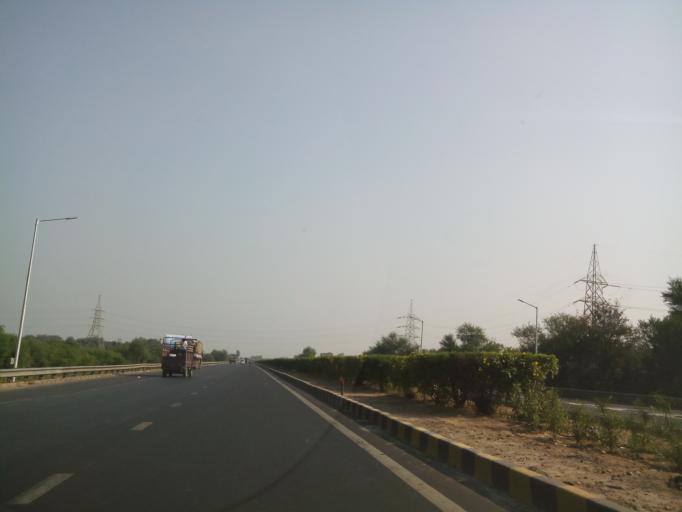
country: IN
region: Gujarat
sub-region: Ahmadabad
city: Ahmedabad
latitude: 22.9687
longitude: 72.6629
